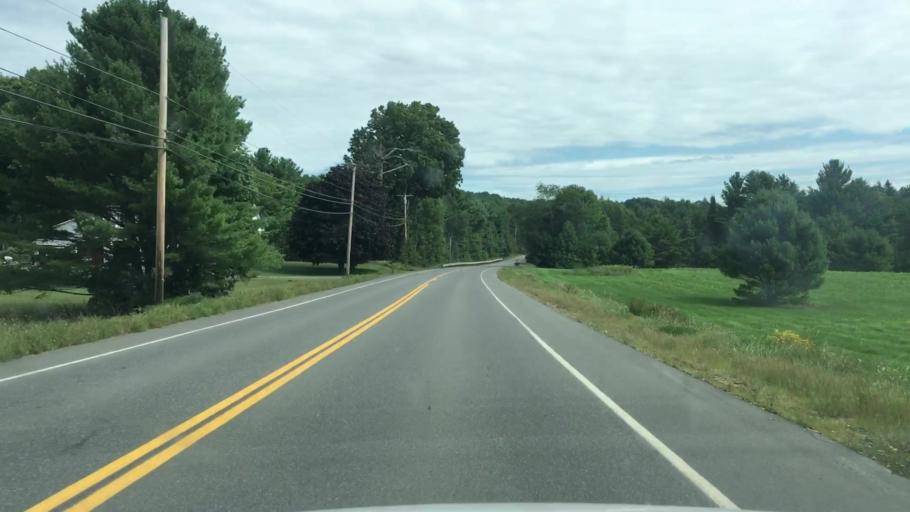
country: US
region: Maine
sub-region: Piscataquis County
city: Dover-Foxcroft
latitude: 45.2053
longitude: -69.1835
